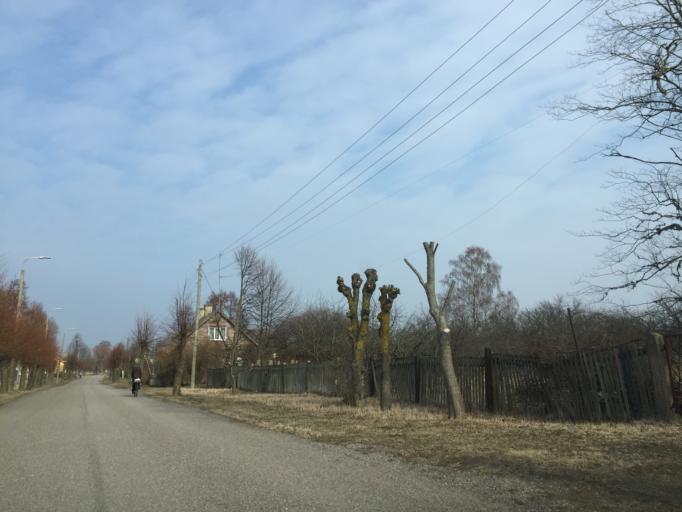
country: LV
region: Salacgrivas
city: Ainazi
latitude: 57.8712
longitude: 24.3608
